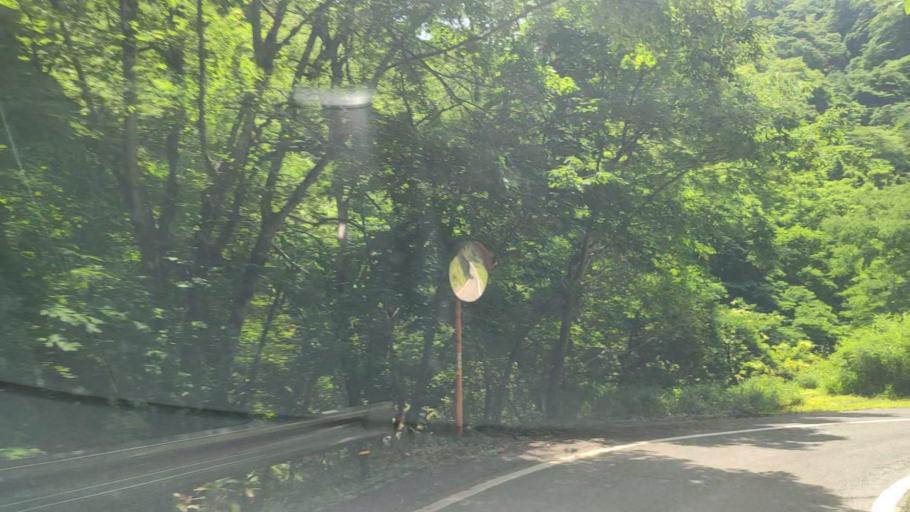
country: JP
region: Tottori
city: Tottori
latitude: 35.4064
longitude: 134.5080
